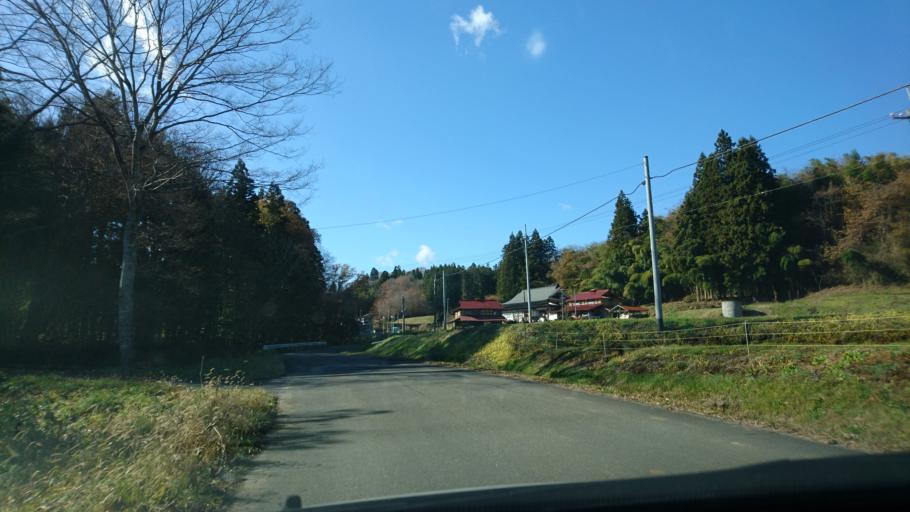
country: JP
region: Iwate
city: Ichinoseki
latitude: 38.9889
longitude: 141.0397
